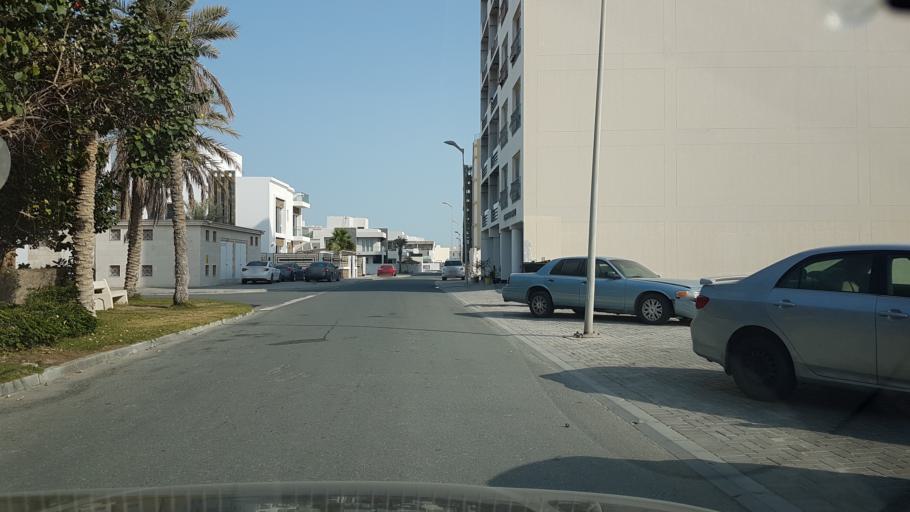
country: BH
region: Muharraq
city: Al Hadd
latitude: 26.2935
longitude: 50.6642
